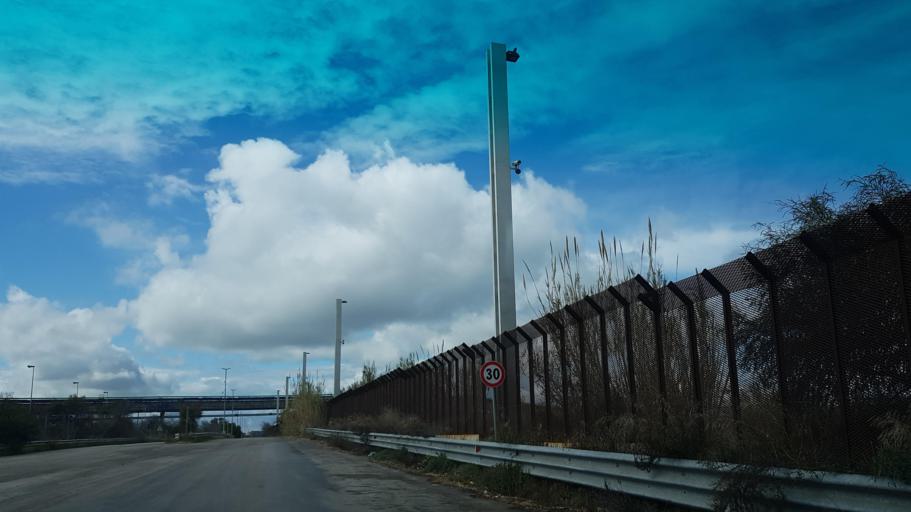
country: IT
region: Apulia
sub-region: Provincia di Brindisi
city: Materdomini
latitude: 40.6447
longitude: 17.9751
